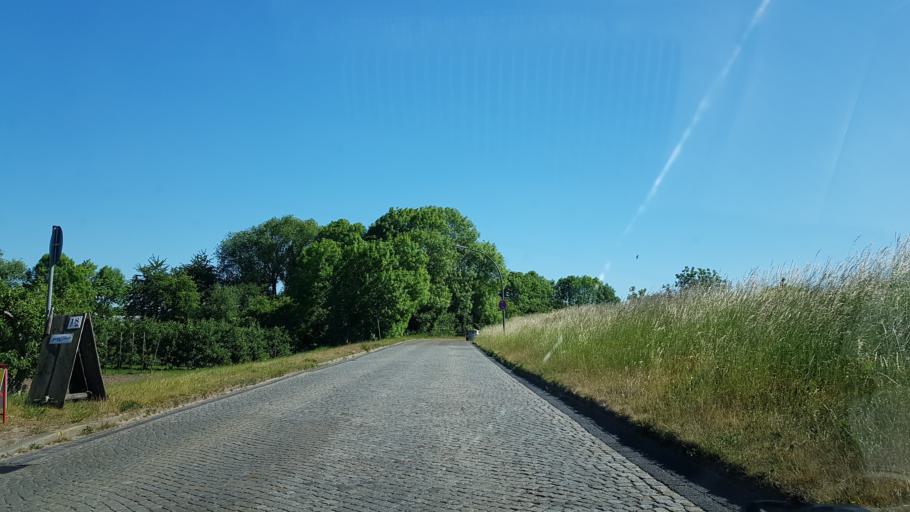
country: DE
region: Lower Saxony
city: Neu Wulmstorf
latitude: 53.5258
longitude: 9.8014
